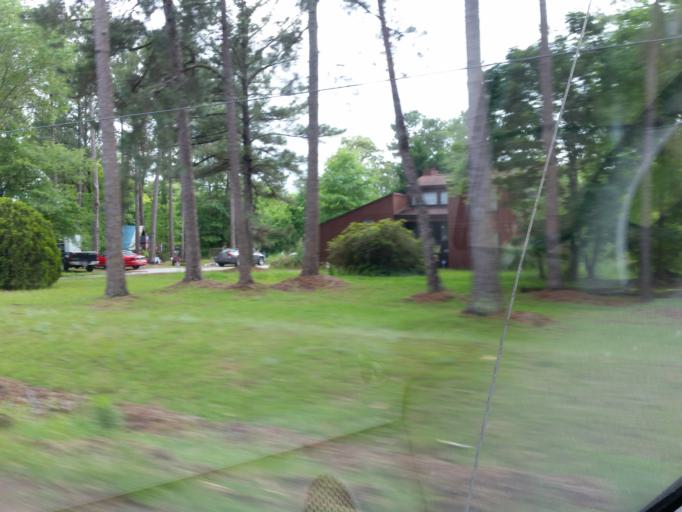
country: US
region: Georgia
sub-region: Dooly County
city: Unadilla
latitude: 32.2975
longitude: -83.7579
